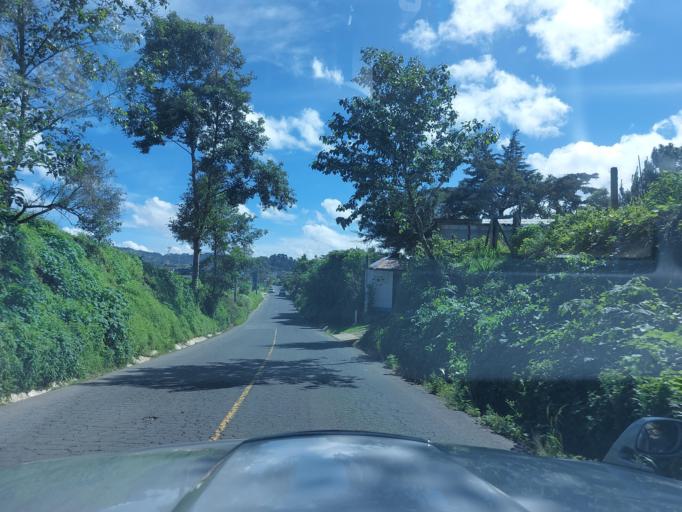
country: GT
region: Chimaltenango
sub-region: Municipio de San Juan Comalapa
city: Comalapa
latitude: 14.7239
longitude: -90.8883
